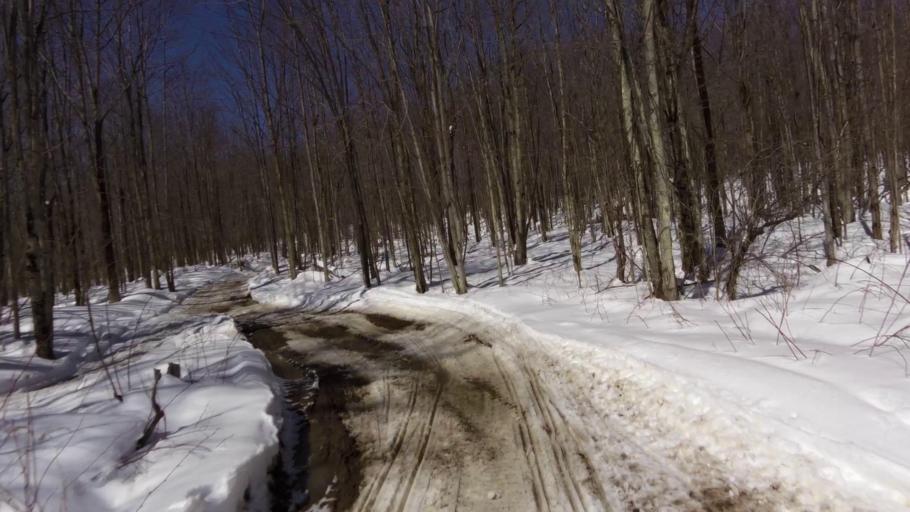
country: US
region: New York
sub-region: Allegany County
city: Houghton
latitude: 42.4008
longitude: -78.2686
